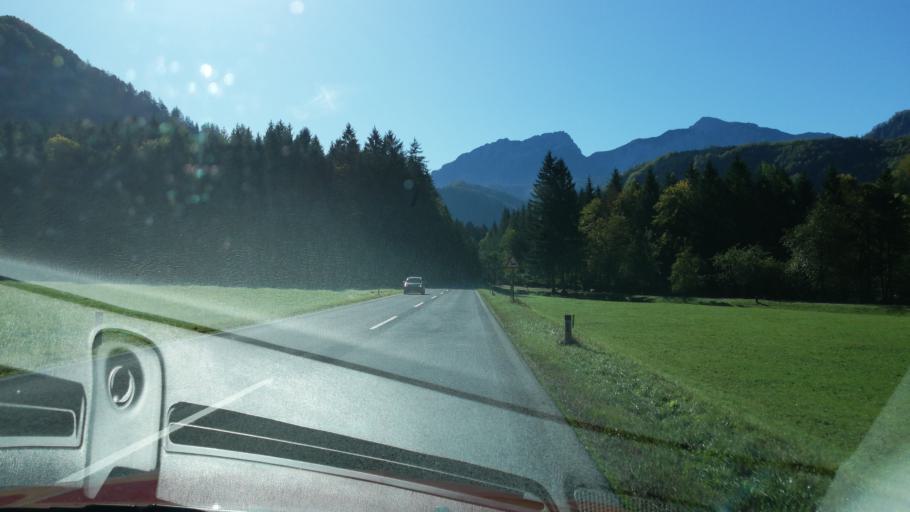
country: AT
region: Styria
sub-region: Politischer Bezirk Liezen
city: Landl
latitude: 47.6826
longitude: 14.7074
